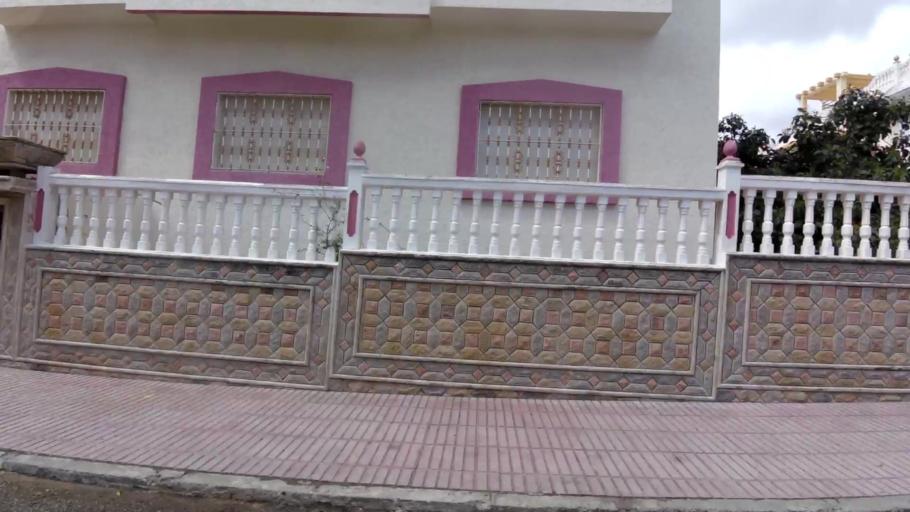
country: MA
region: Tanger-Tetouan
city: Tetouan
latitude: 35.5905
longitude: -5.3418
